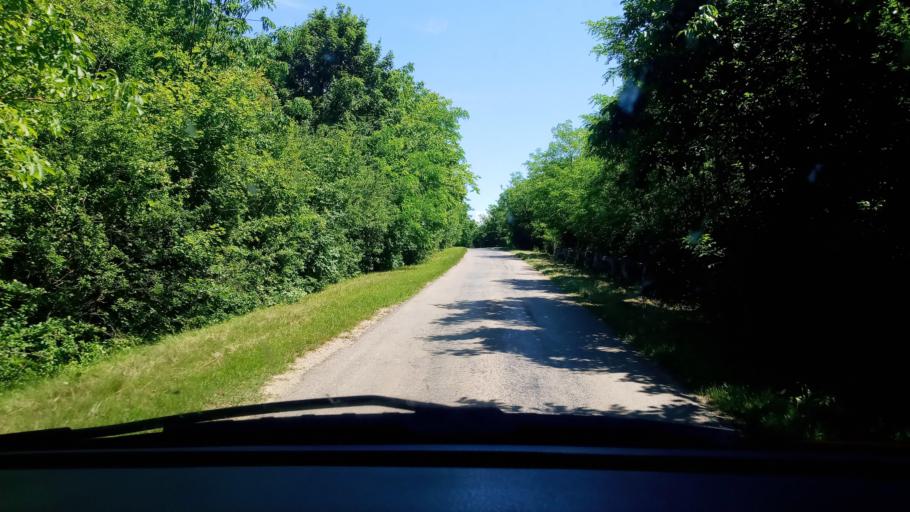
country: HU
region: Somogy
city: Kadarkut
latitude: 46.1783
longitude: 17.7400
